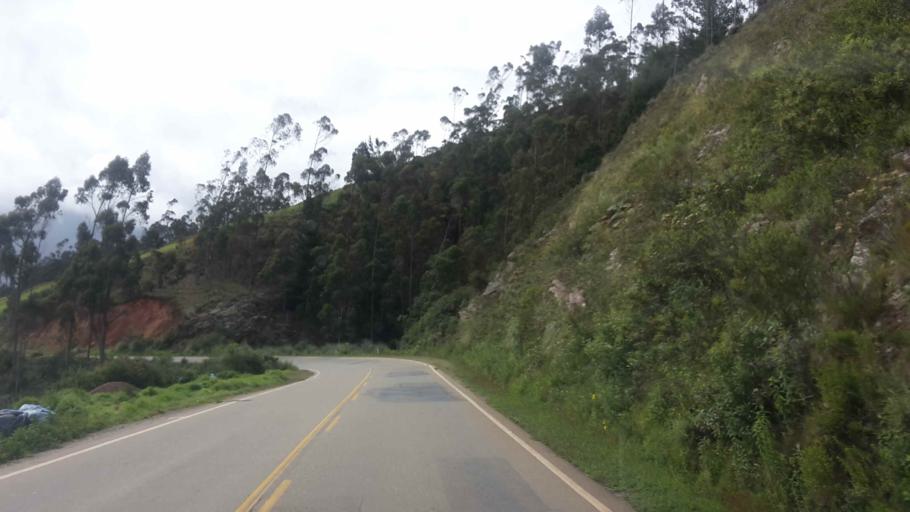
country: BO
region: Cochabamba
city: Totora
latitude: -17.5531
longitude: -65.3483
